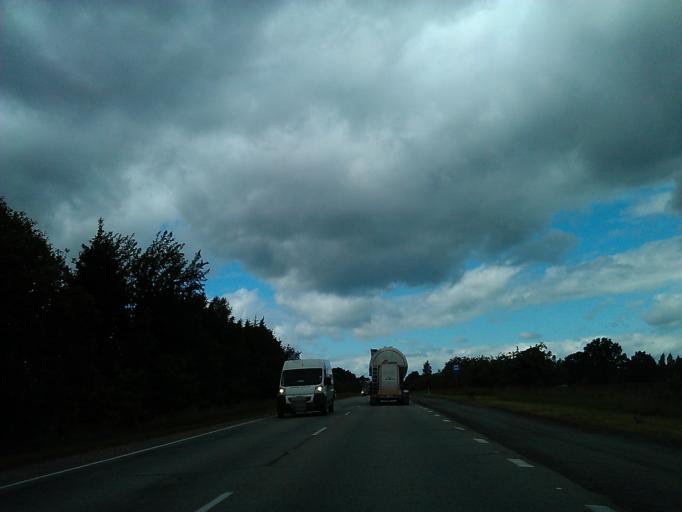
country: LV
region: Tukuma Rajons
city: Tukums
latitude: 56.9283
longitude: 23.2218
